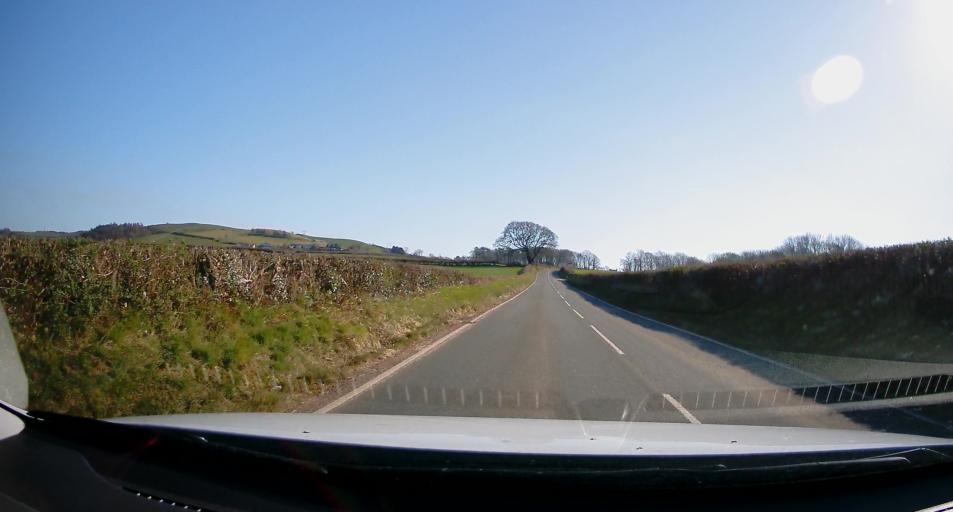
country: GB
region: Wales
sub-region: County of Ceredigion
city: Penparcau
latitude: 52.3592
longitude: -4.0582
